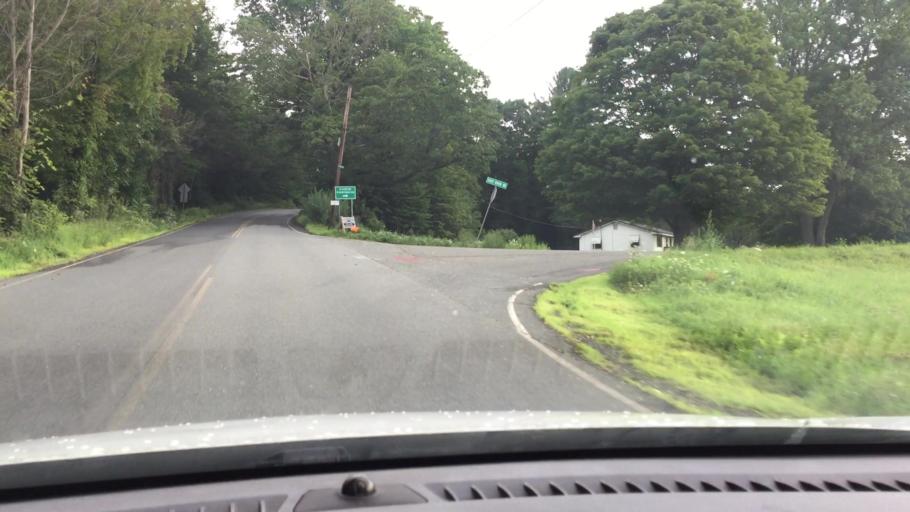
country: US
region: Massachusetts
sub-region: Hampshire County
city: Chesterfield
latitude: 42.2746
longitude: -72.9141
